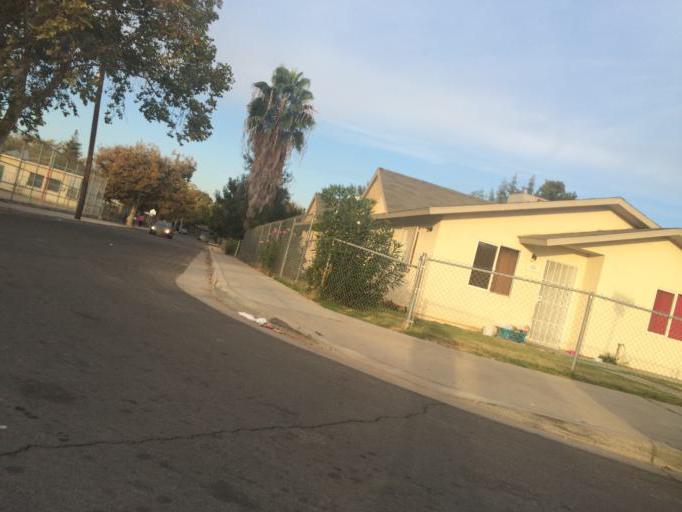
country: US
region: California
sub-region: Fresno County
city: Fresno
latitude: 36.7459
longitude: -119.7771
